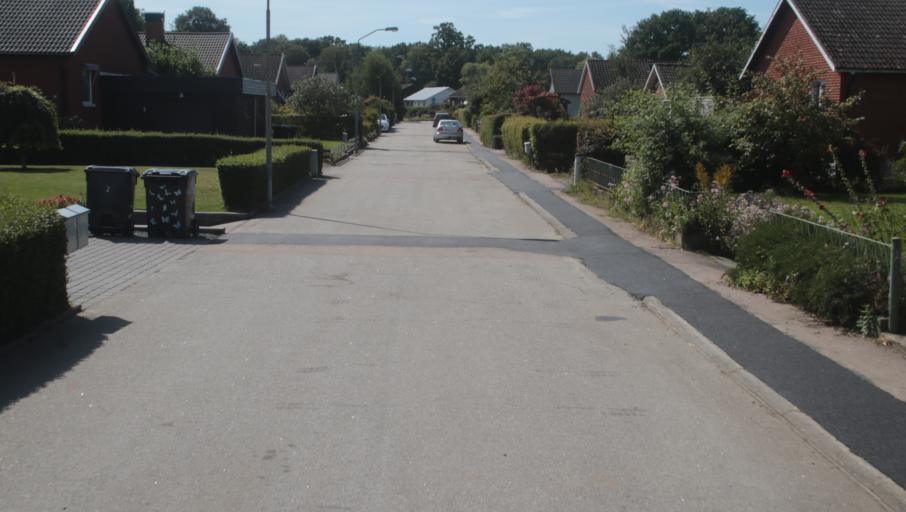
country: SE
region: Blekinge
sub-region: Karlshamns Kommun
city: Karlshamn
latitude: 56.2004
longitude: 14.8283
